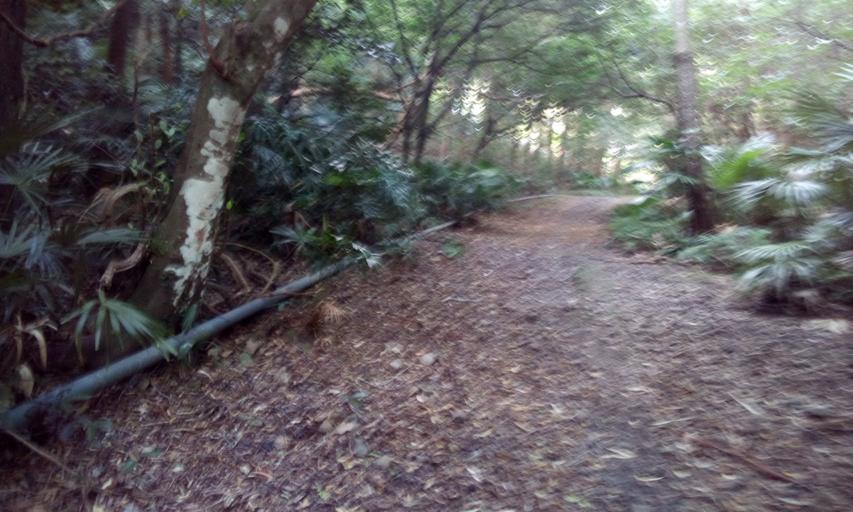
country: AU
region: New South Wales
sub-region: Wollongong
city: Cordeaux Heights
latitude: -34.4410
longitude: 150.8130
